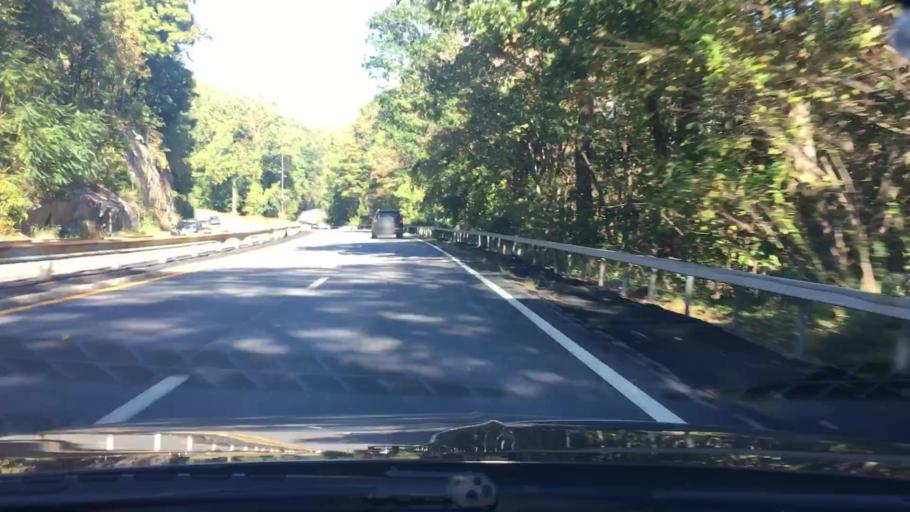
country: US
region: New York
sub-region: Westchester County
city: Chappaqua
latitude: 41.1654
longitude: -73.7700
